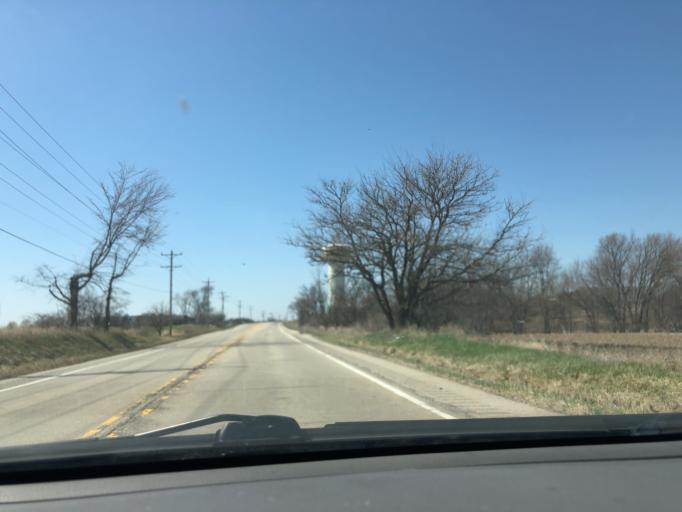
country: US
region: Illinois
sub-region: Kane County
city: Hampshire
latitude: 42.1342
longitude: -88.4976
